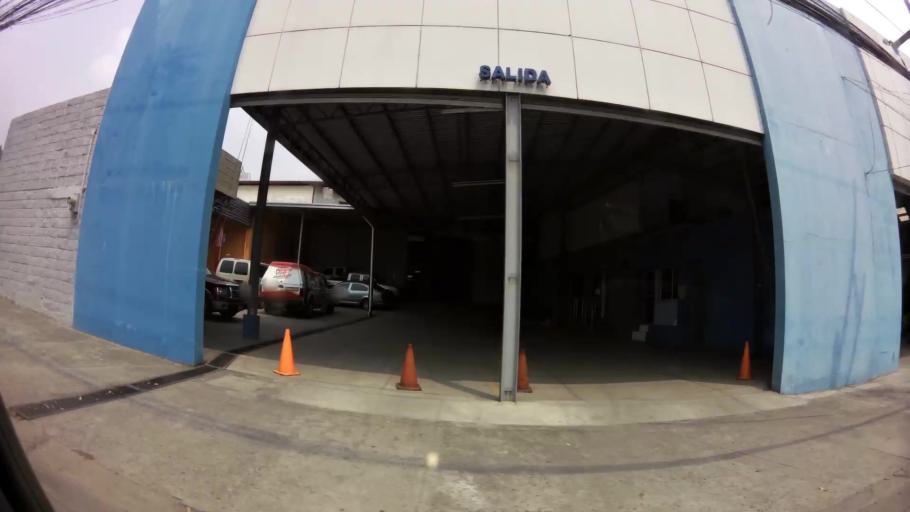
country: HN
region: Cortes
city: San Pedro Sula
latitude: 15.4867
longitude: -88.0285
